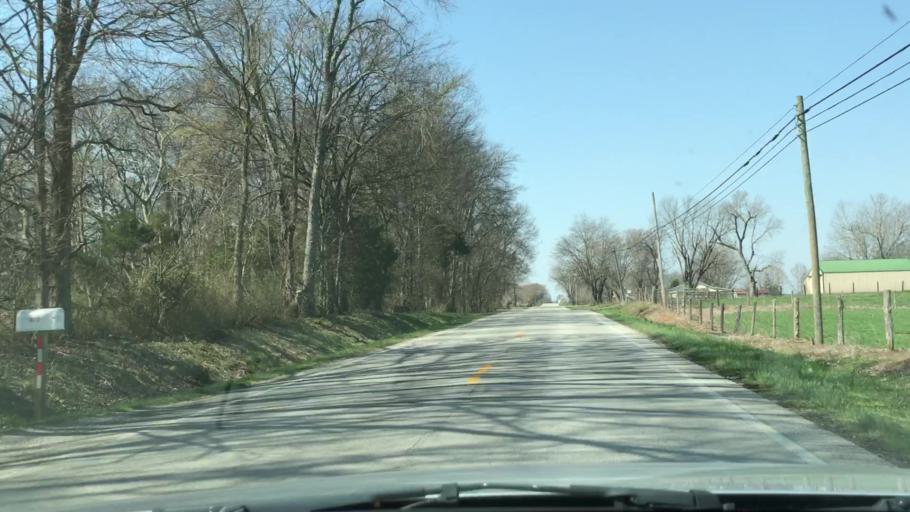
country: US
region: Kentucky
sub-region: Edmonson County
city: Brownsville
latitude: 37.0922
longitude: -86.1389
